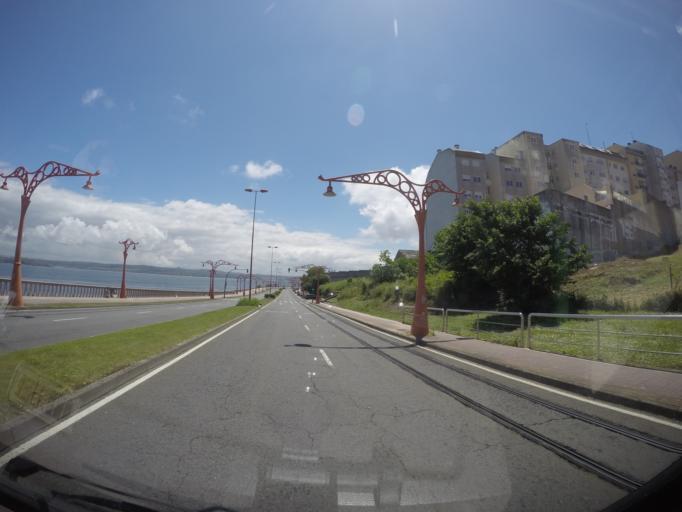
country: ES
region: Galicia
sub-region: Provincia da Coruna
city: A Coruna
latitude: 43.3803
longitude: -8.3967
